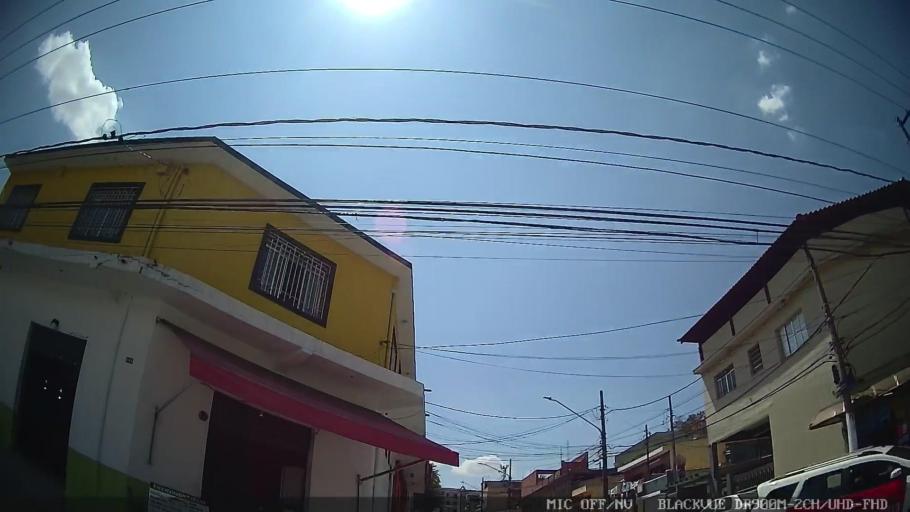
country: BR
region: Sao Paulo
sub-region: Guarulhos
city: Guarulhos
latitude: -23.5213
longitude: -46.4897
